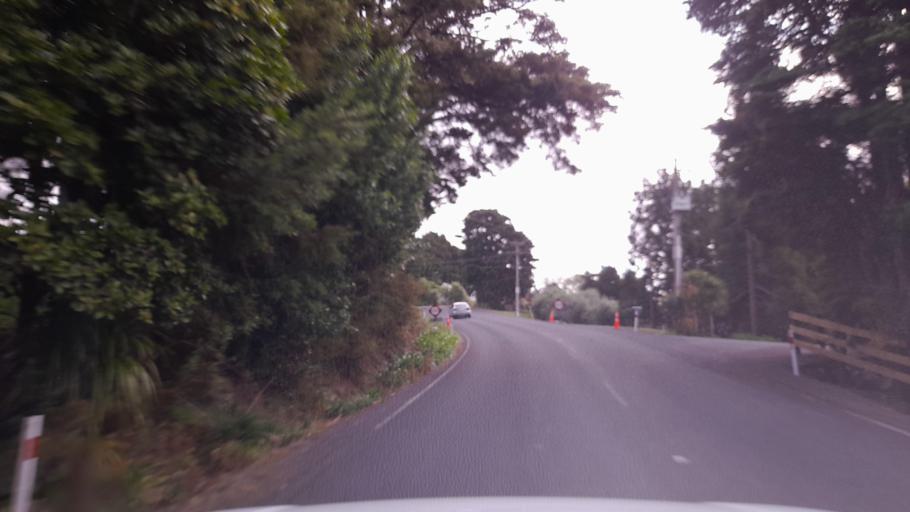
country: NZ
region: Northland
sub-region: Whangarei
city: Maungatapere
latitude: -35.7522
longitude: 174.2481
